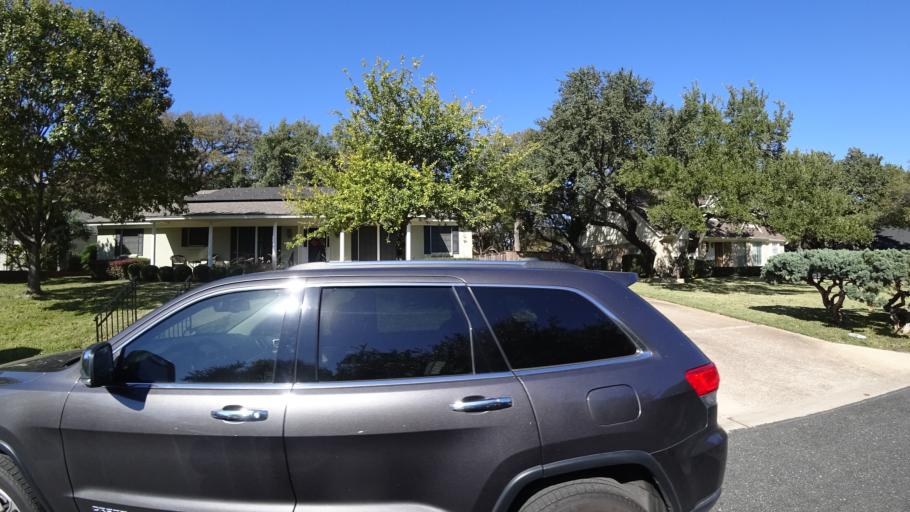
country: US
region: Texas
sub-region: Williamson County
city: Jollyville
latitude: 30.3782
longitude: -97.7464
